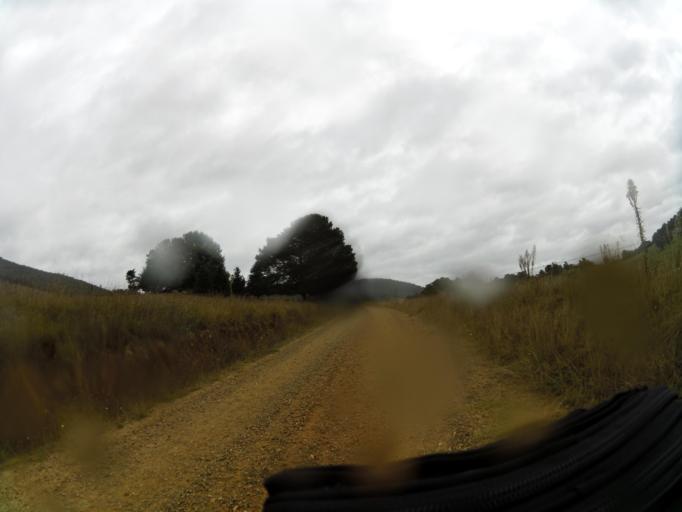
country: AU
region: New South Wales
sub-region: Greater Hume Shire
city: Holbrook
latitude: -36.2361
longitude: 147.6241
